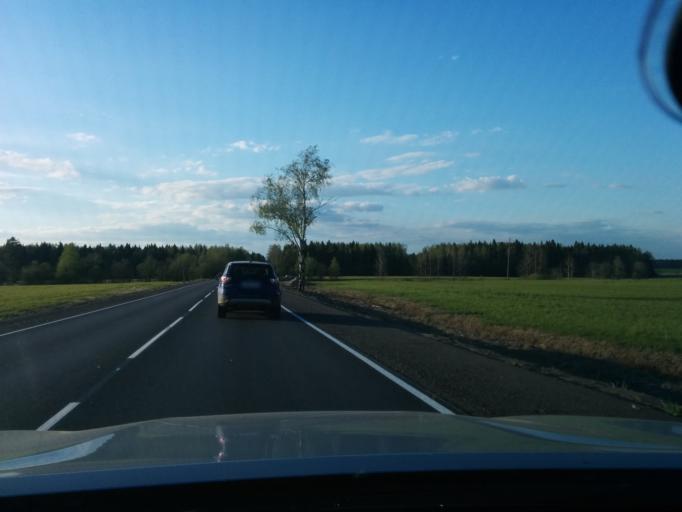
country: RU
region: Leningrad
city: Verkhniye Osel'ki
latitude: 60.2017
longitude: 30.4265
